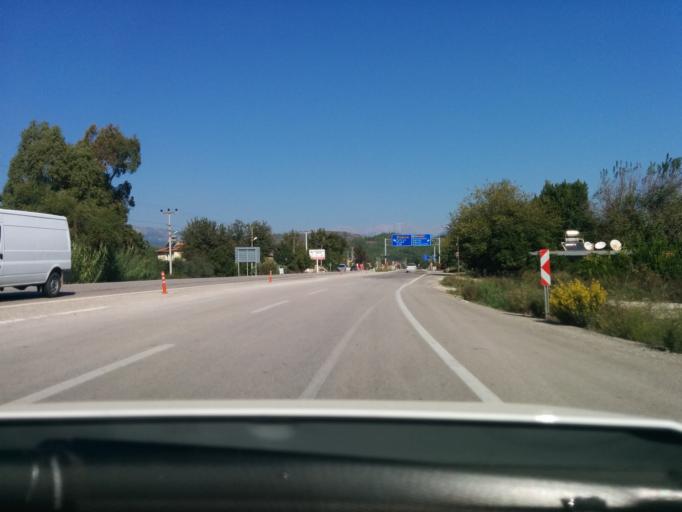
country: TR
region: Mugla
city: Kemer
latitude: 36.6298
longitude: 29.3560
